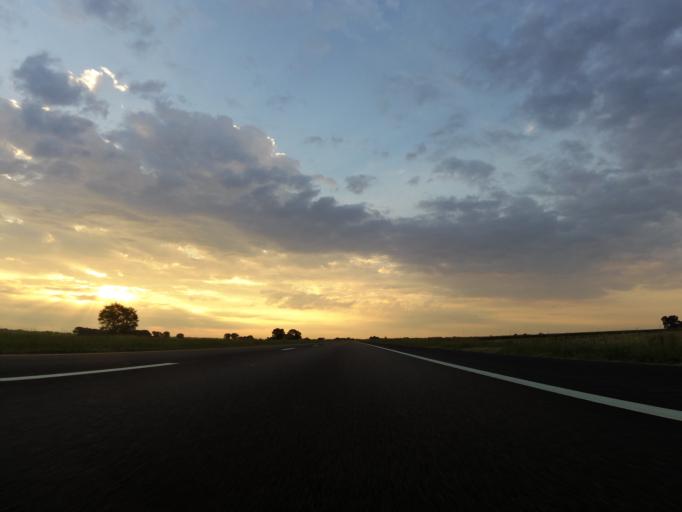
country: US
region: Kansas
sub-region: Sedgwick County
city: Colwich
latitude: 37.8445
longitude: -97.5844
